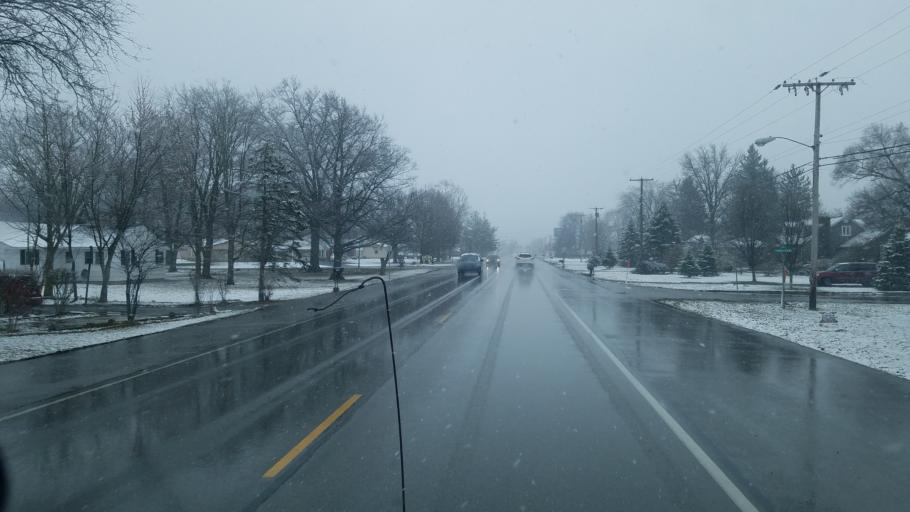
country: US
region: Indiana
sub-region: Grant County
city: Marion
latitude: 40.5796
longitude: -85.6779
